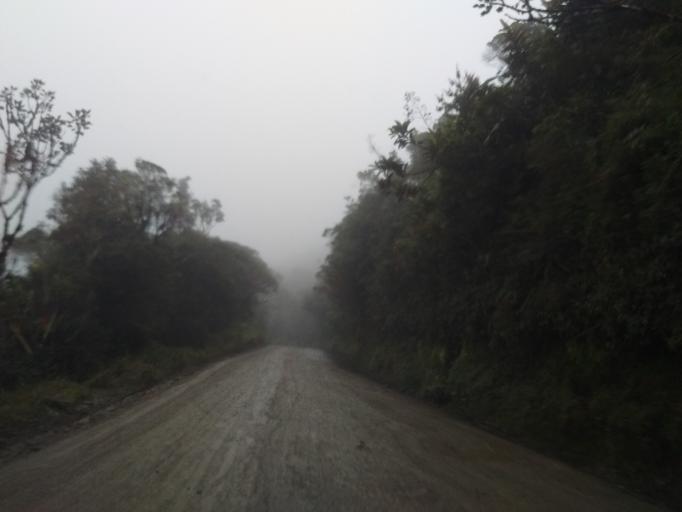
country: CO
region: Cauca
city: Paispamba
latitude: 2.1490
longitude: -76.4465
